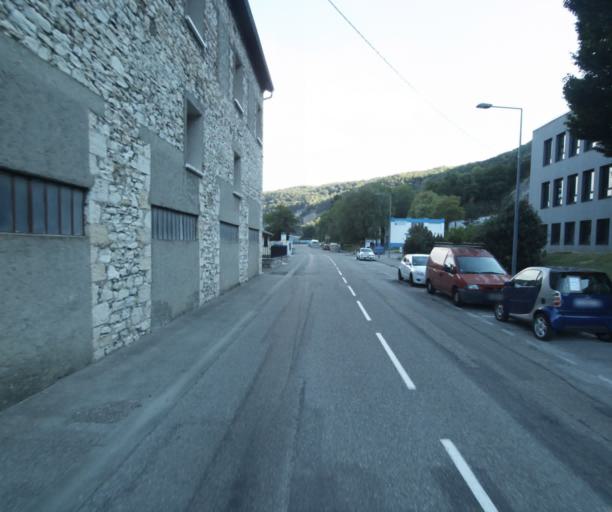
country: FR
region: Rhone-Alpes
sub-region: Departement de l'Isere
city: Sassenage
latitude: 45.2005
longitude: 5.6647
